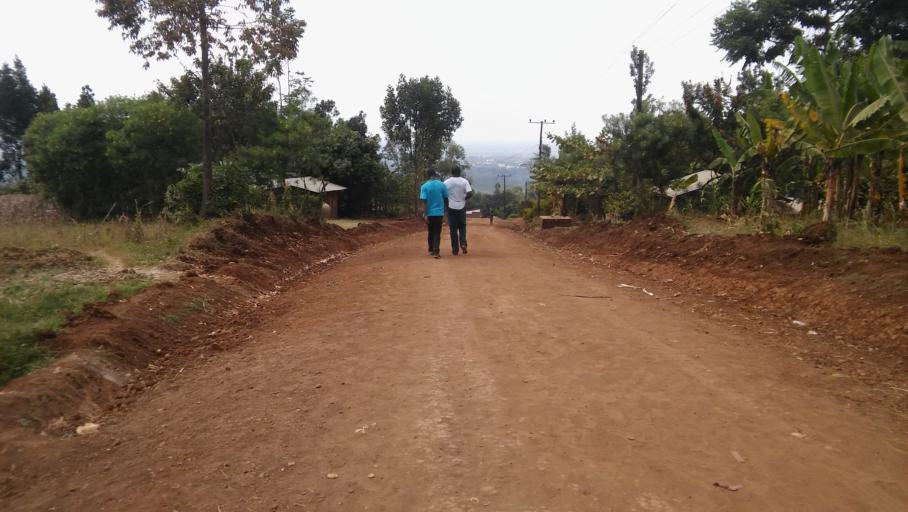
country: UG
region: Eastern Region
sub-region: Mbale District
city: Mbale
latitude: 1.0578
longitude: 34.2135
